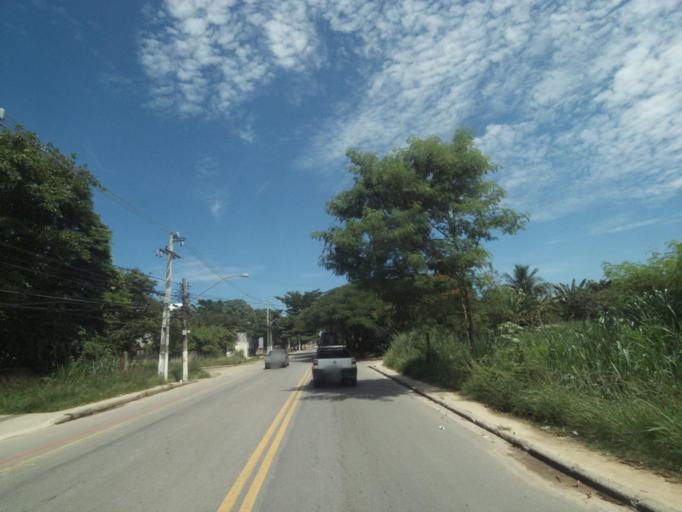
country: BR
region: Rio de Janeiro
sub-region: Niteroi
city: Niteroi
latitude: -22.9363
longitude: -43.0118
